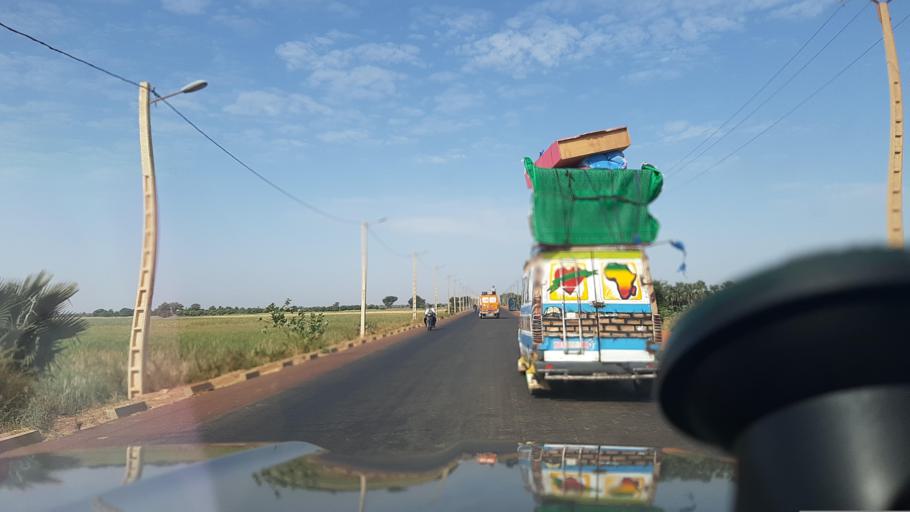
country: ML
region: Segou
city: Markala
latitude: 13.6833
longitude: -6.0912
